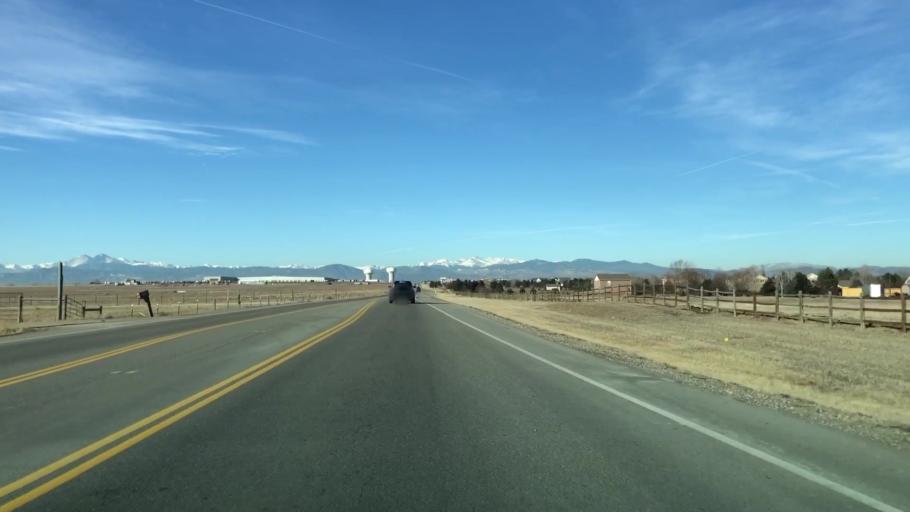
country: US
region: Colorado
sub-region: Weld County
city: Windsor
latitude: 40.4359
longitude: -104.9462
